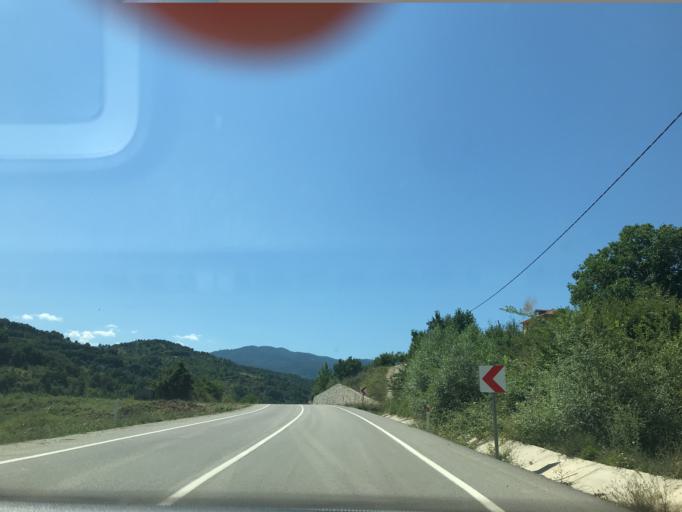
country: TR
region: Bursa
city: Tahtakopru
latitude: 39.9758
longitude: 29.6046
